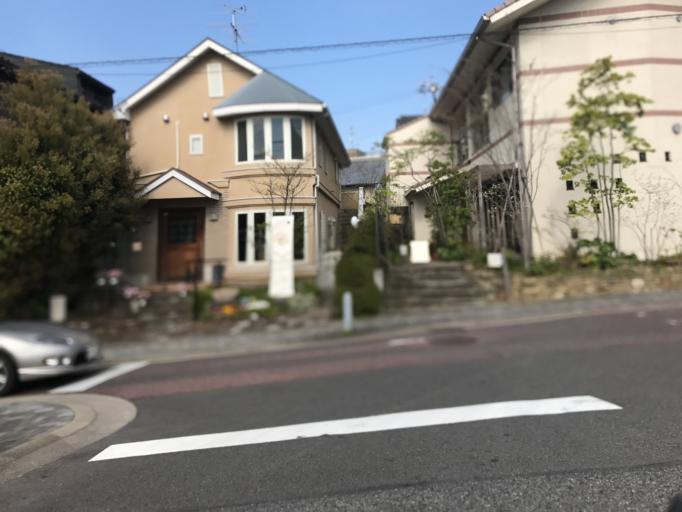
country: JP
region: Aichi
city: Nagoya-shi
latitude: 35.1702
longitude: 136.9541
